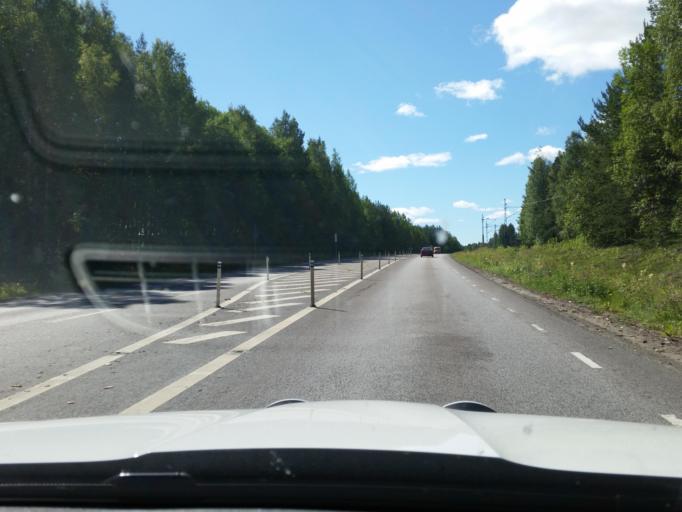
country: SE
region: Norrbotten
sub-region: Pitea Kommun
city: Pitea
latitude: 65.2973
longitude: 21.5100
